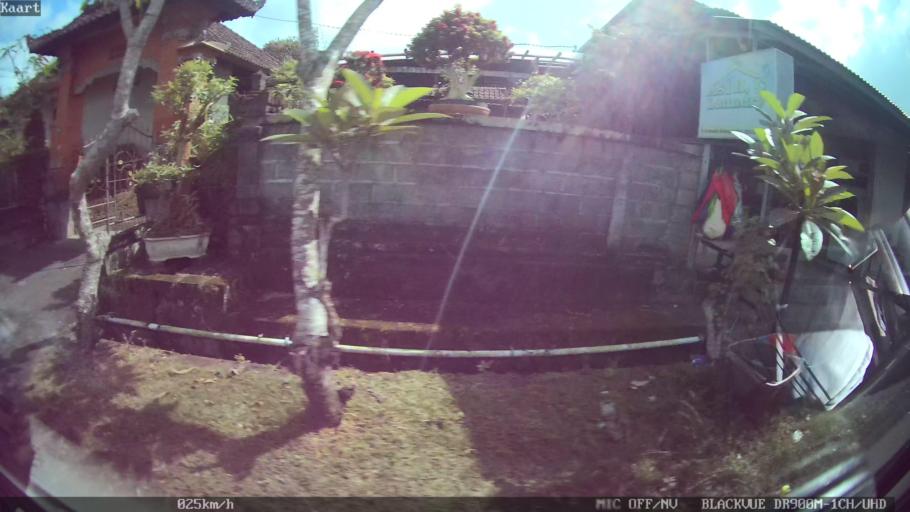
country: ID
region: Bali
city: Banjar Batur
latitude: -8.5968
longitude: 115.2094
